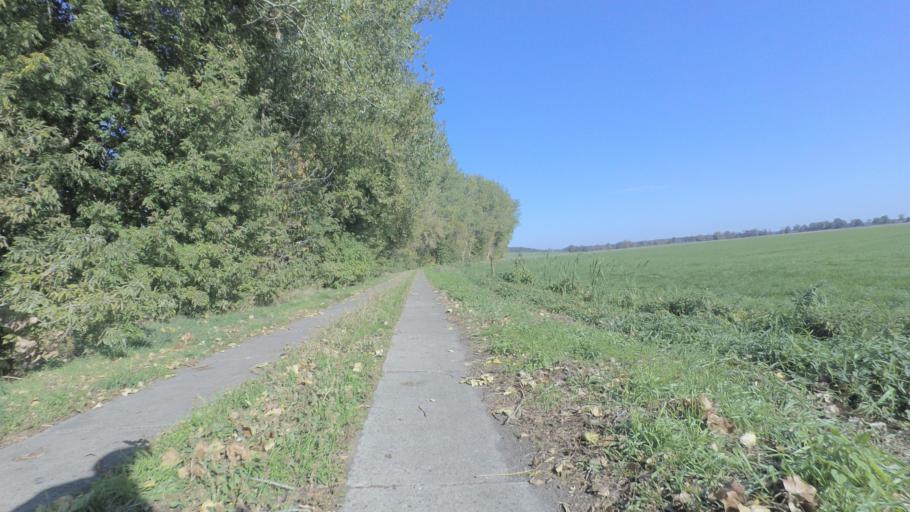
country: DE
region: Brandenburg
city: Rangsdorf
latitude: 52.2855
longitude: 13.3580
